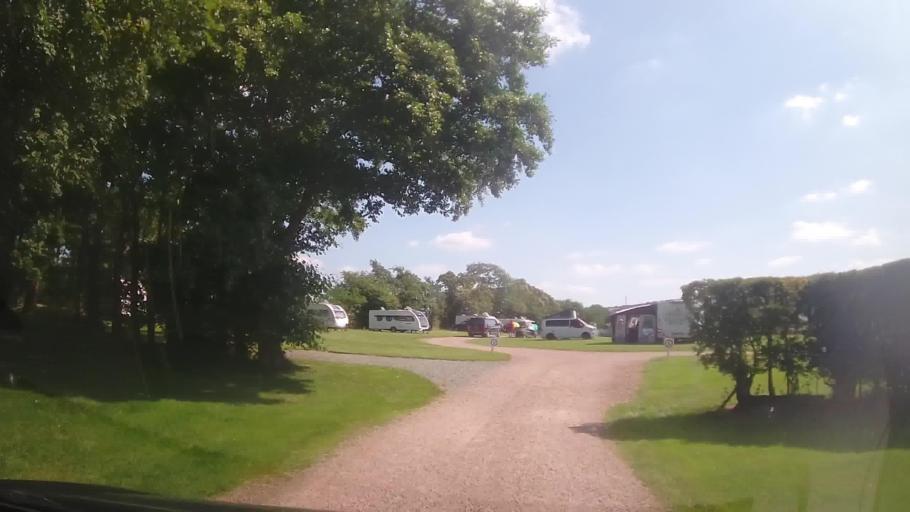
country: GB
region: England
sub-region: Herefordshire
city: Ocle Pychard
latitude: 52.0655
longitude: -2.5441
